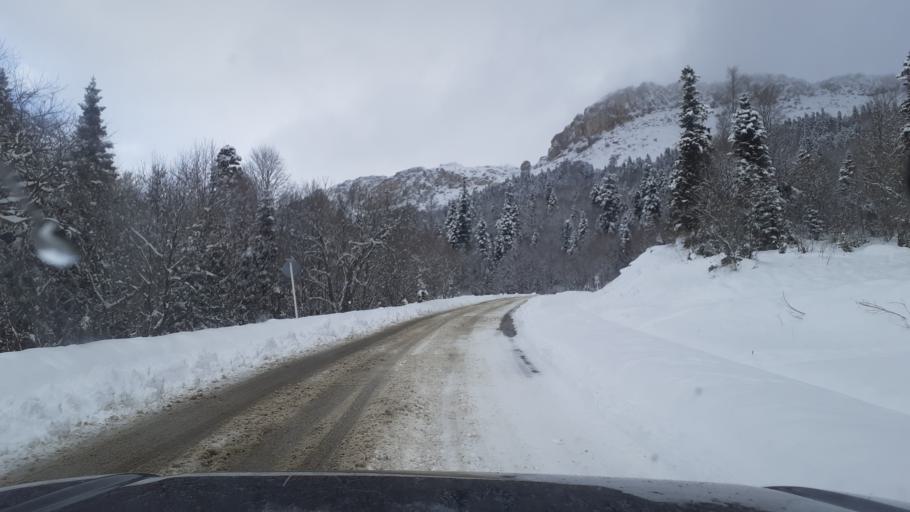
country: RU
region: Adygeya
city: Kamennomostskiy
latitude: 44.0083
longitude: 40.0109
